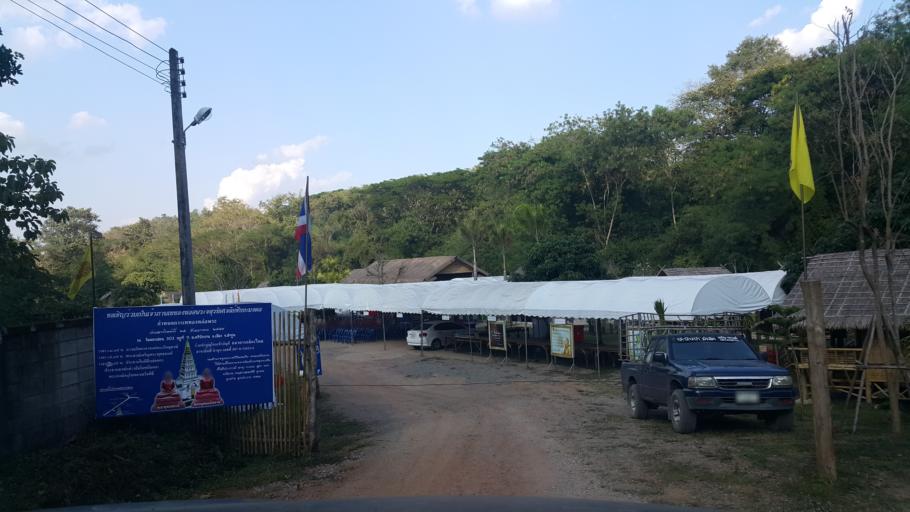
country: TH
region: Lamphun
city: Mae Tha
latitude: 18.5135
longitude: 99.0987
